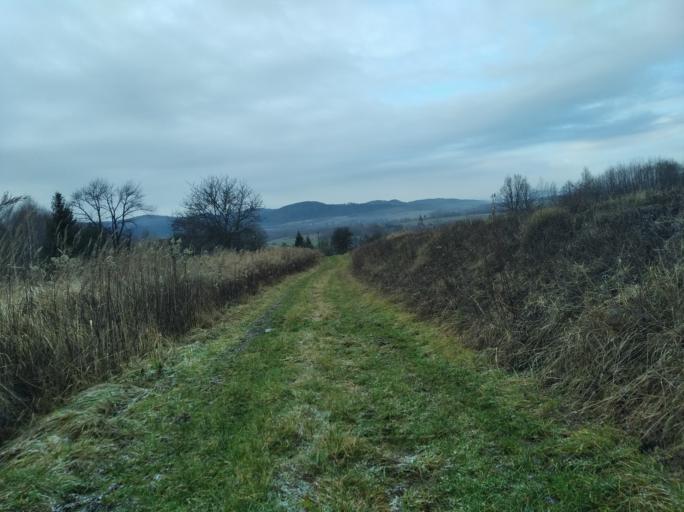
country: PL
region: Subcarpathian Voivodeship
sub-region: Powiat strzyzowski
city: Wysoka Strzyzowska
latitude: 49.8312
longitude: 21.7527
